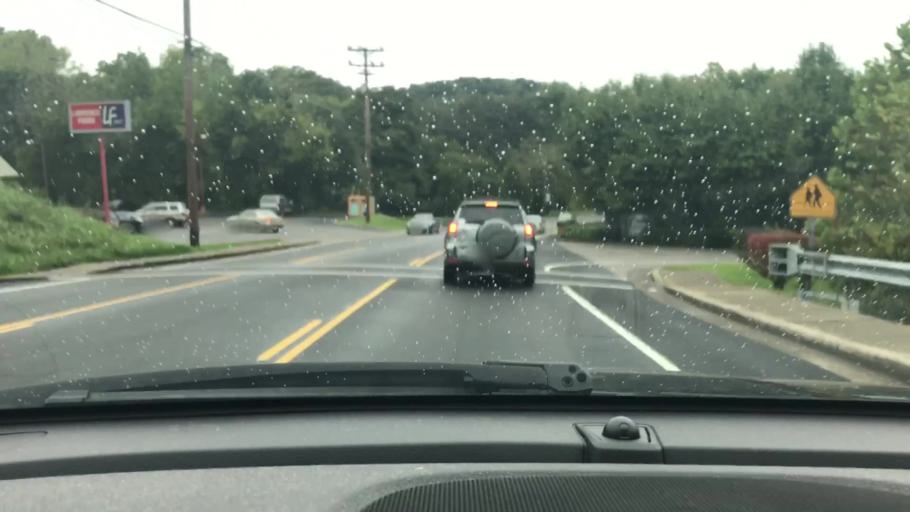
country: US
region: Tennessee
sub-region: Cheatham County
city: Kingston Springs
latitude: 36.0878
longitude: -87.1042
